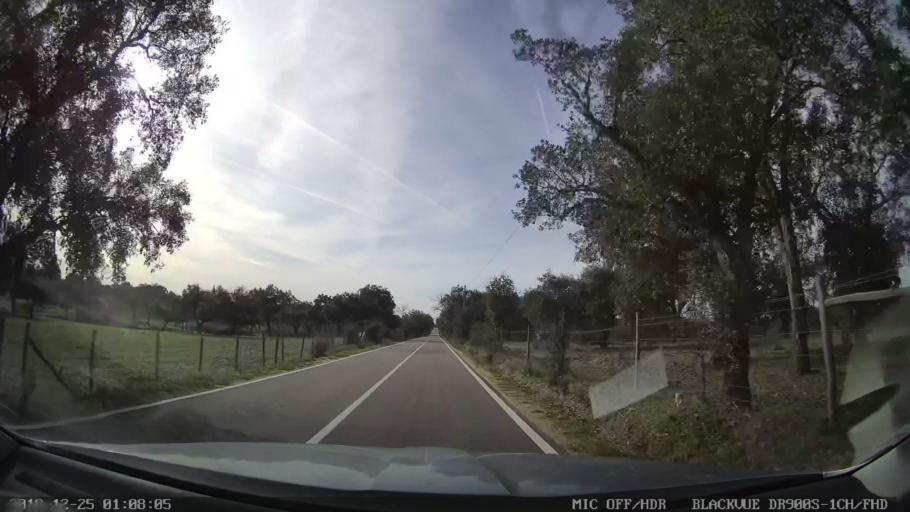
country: PT
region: Portalegre
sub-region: Nisa
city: Nisa
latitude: 39.4546
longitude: -7.7092
